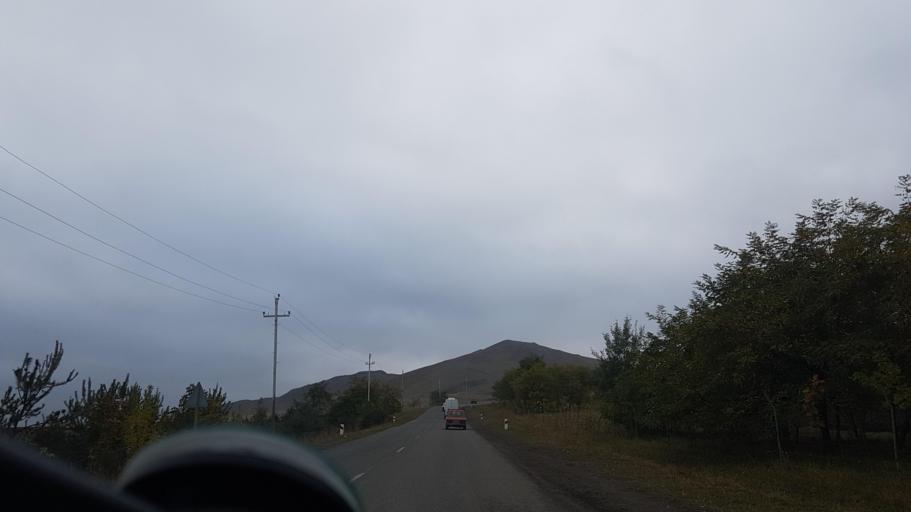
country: AZ
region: Gadabay Rayon
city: Ariqdam
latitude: 40.6285
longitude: 45.8150
